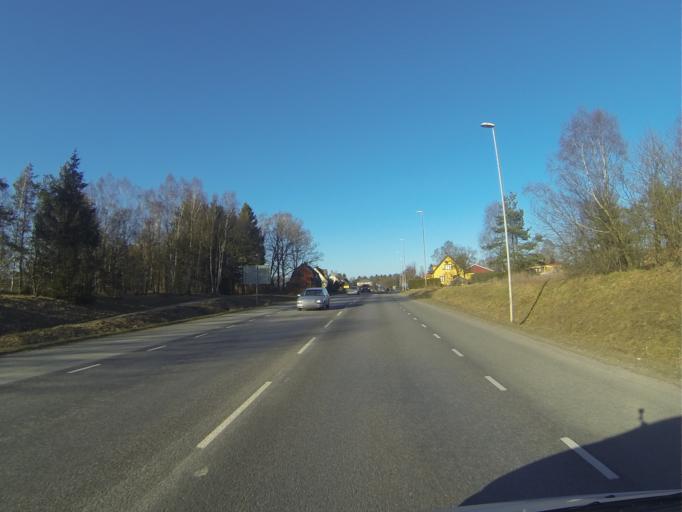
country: SE
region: Skane
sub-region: Hoors Kommun
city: Hoeoer
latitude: 55.9377
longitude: 13.5568
